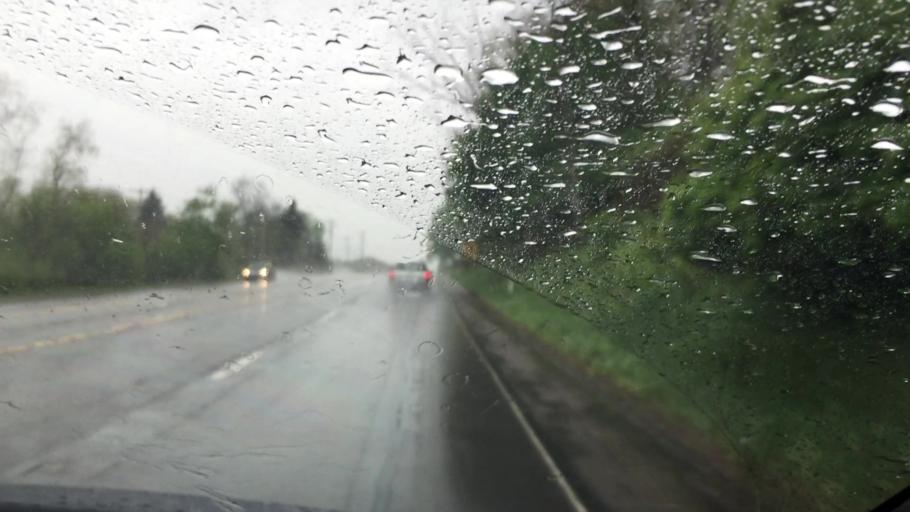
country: US
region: Pennsylvania
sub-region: Butler County
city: Nixon
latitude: 40.7484
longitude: -79.9251
